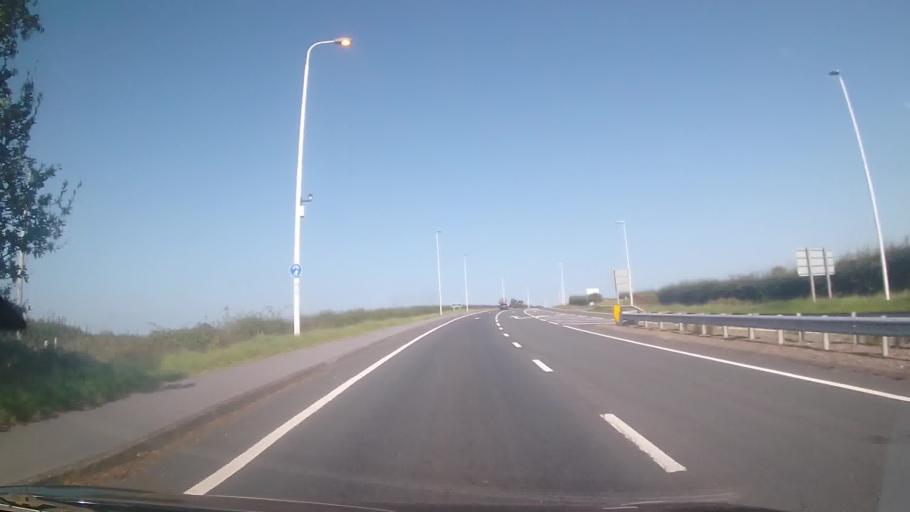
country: GB
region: Wales
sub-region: County of Ceredigion
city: Cardigan
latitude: 52.0906
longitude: -4.6433
